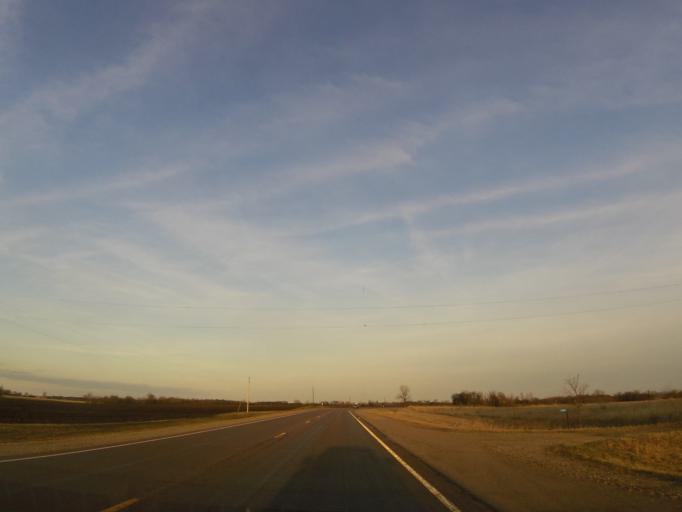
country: US
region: Minnesota
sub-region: Carver County
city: Norwood (historical)
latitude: 44.6769
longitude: -93.9658
